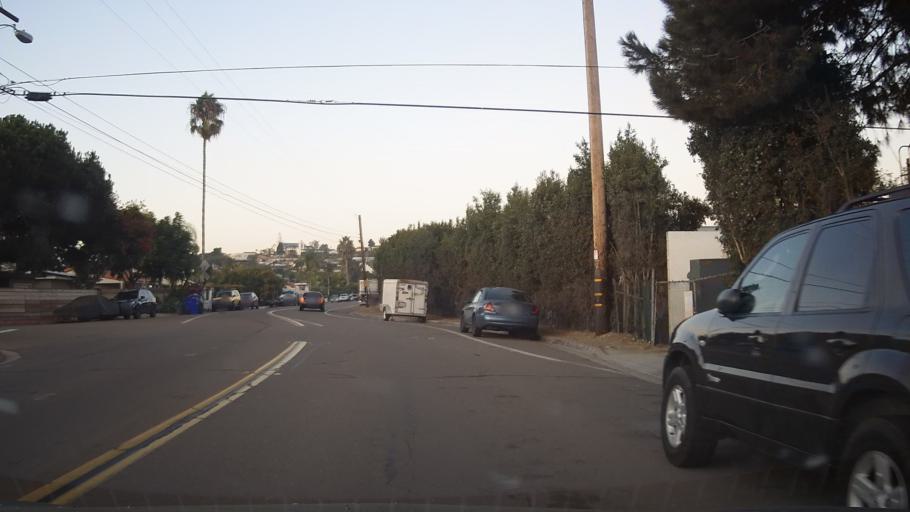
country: US
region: California
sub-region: San Diego County
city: San Diego
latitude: 32.7746
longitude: -117.2044
